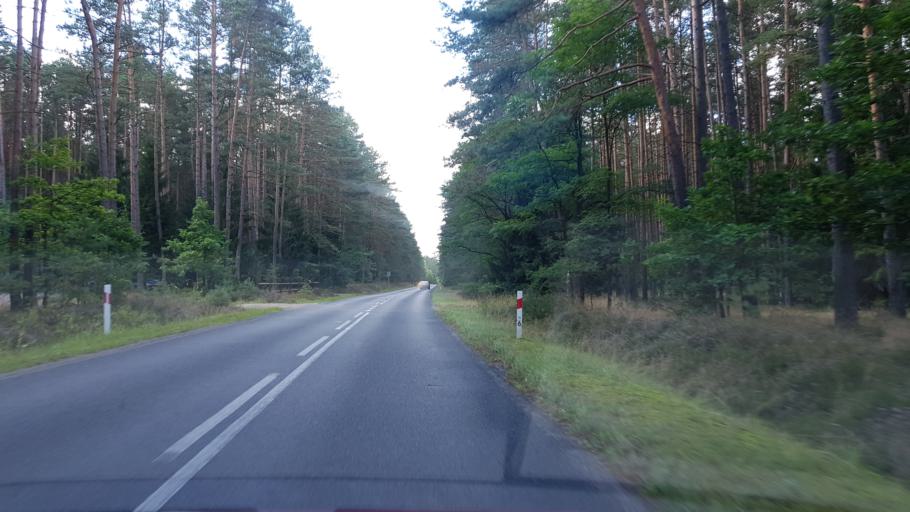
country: PL
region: West Pomeranian Voivodeship
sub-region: Powiat koszalinski
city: Sianow
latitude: 54.0931
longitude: 16.3486
